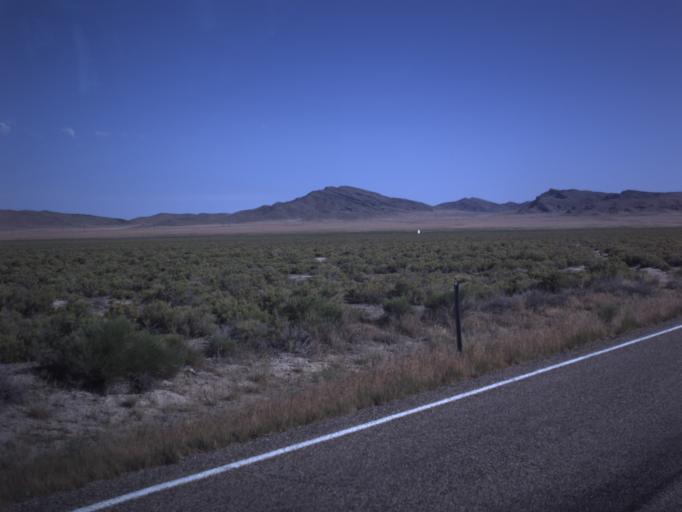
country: US
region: Utah
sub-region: Beaver County
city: Milford
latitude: 38.7041
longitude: -112.9716
